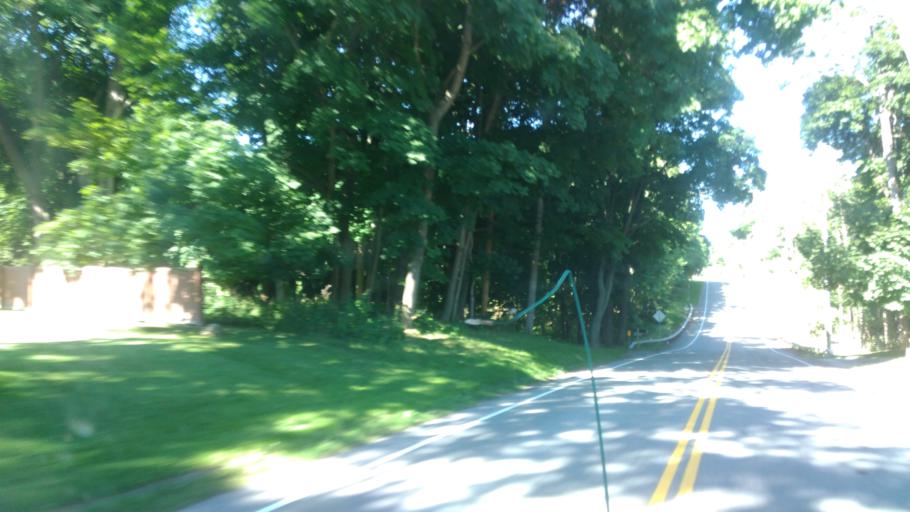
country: US
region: New York
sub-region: Monroe County
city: Webster
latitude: 43.2589
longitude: -77.4562
